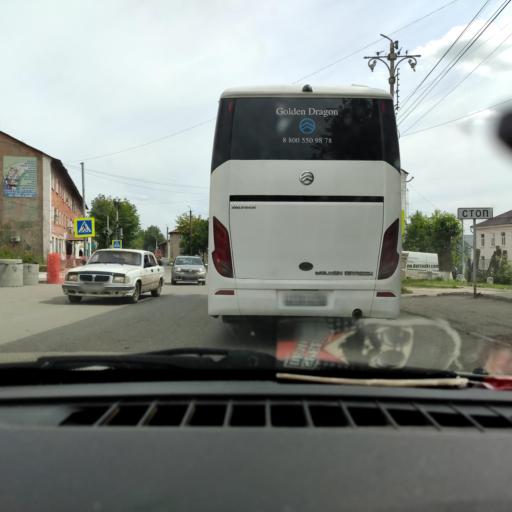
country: RU
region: Perm
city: Chusovoy
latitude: 58.2976
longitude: 57.8193
